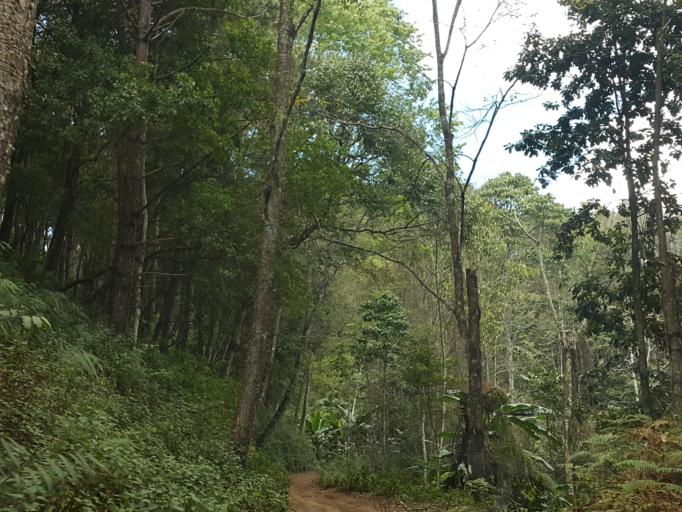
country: TH
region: Chiang Mai
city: Wiang Haeng
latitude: 19.5513
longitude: 98.8148
